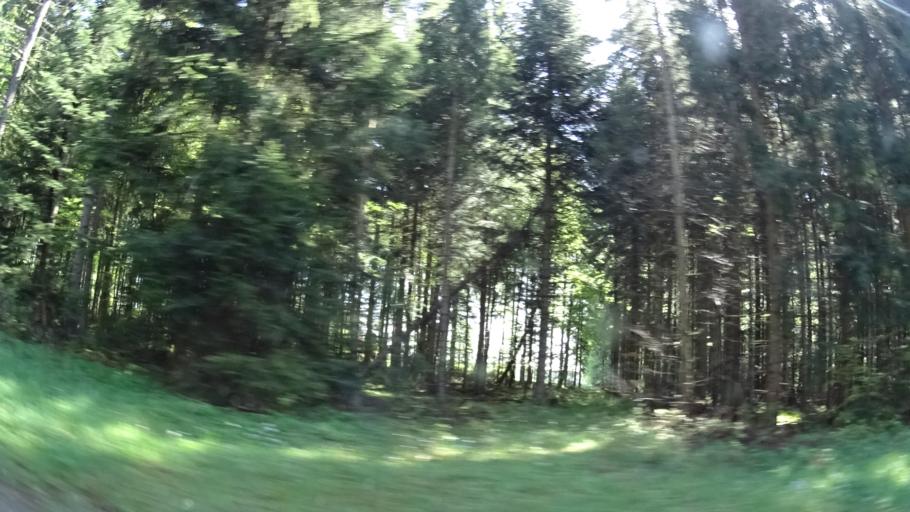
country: DE
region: Baden-Wuerttemberg
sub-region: Karlsruhe Region
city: Neuweiler
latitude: 48.6589
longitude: 8.5658
